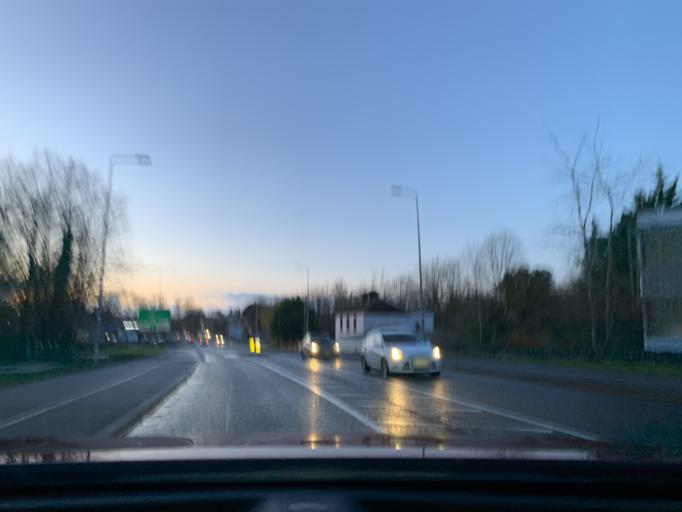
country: IE
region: Connaught
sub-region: County Leitrim
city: Carrick-on-Shannon
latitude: 53.9455
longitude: -8.0755
